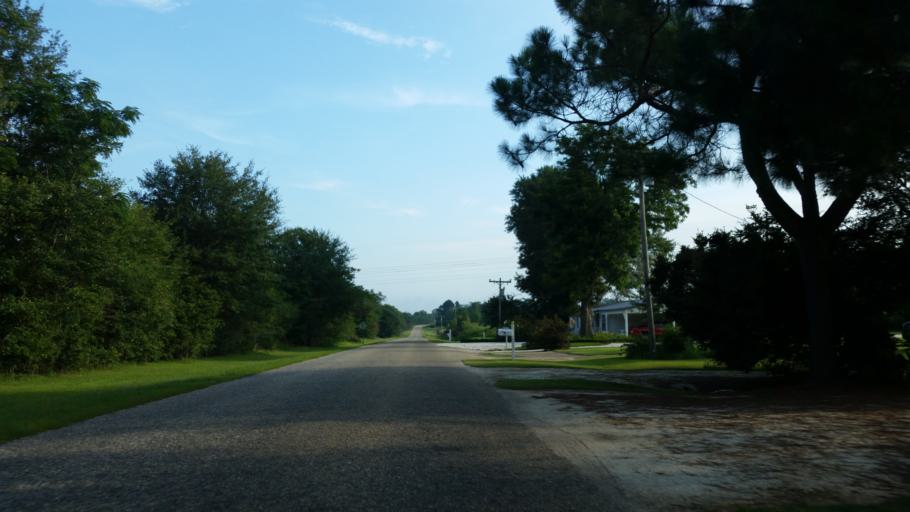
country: US
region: Alabama
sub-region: Escambia County
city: Atmore
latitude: 30.9984
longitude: -87.5685
